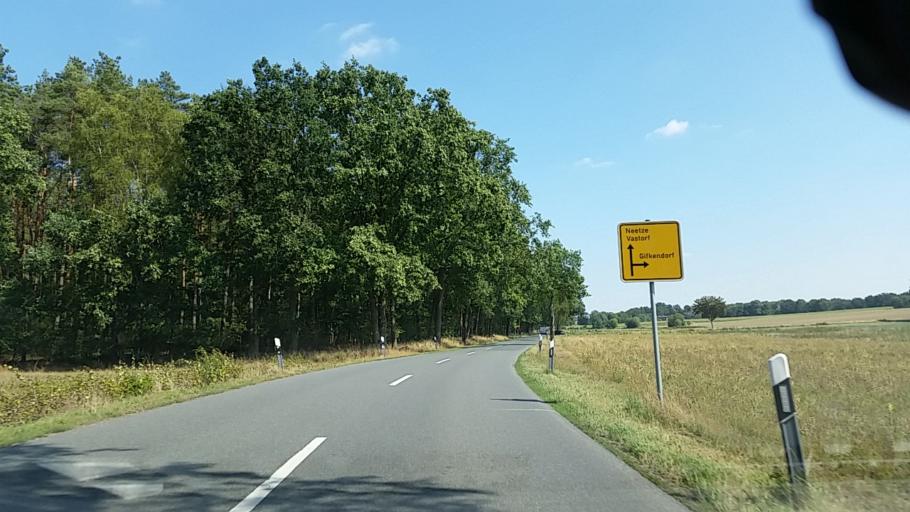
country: DE
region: Lower Saxony
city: Vastorf
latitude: 53.1893
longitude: 10.5334
